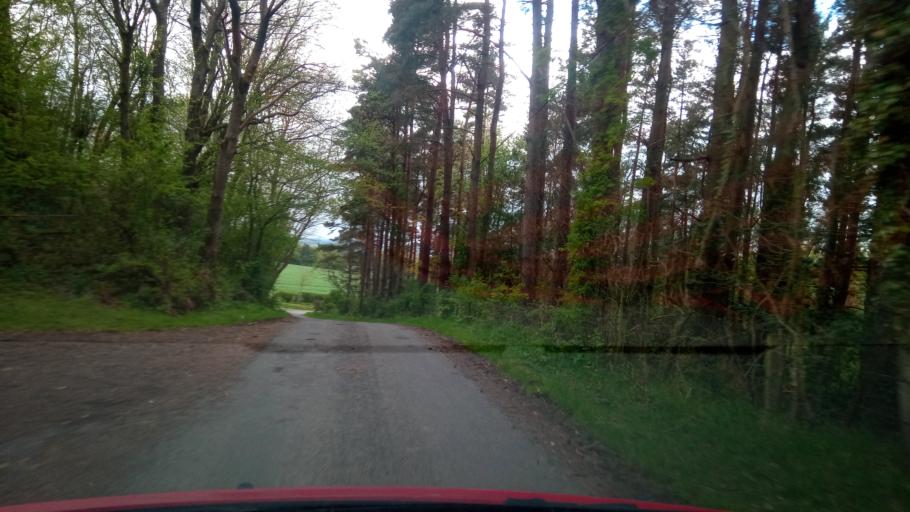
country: GB
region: Scotland
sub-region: The Scottish Borders
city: Saint Boswells
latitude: 55.5087
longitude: -2.6563
